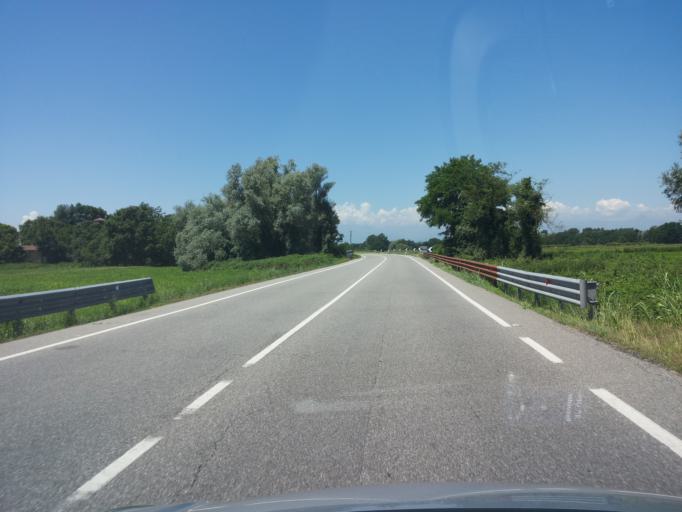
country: IT
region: Piedmont
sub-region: Provincia di Vercelli
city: Quinto Vercellese
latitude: 45.3800
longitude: 8.3663
